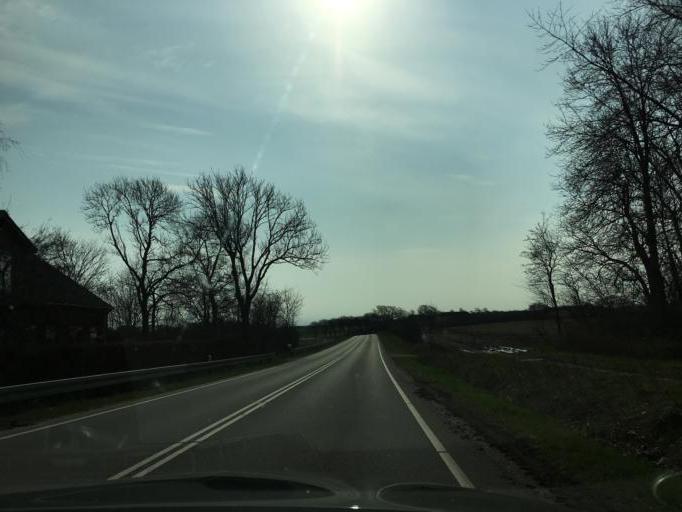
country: DK
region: South Denmark
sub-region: Vejen Kommune
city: Brorup
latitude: 55.4964
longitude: 9.0422
